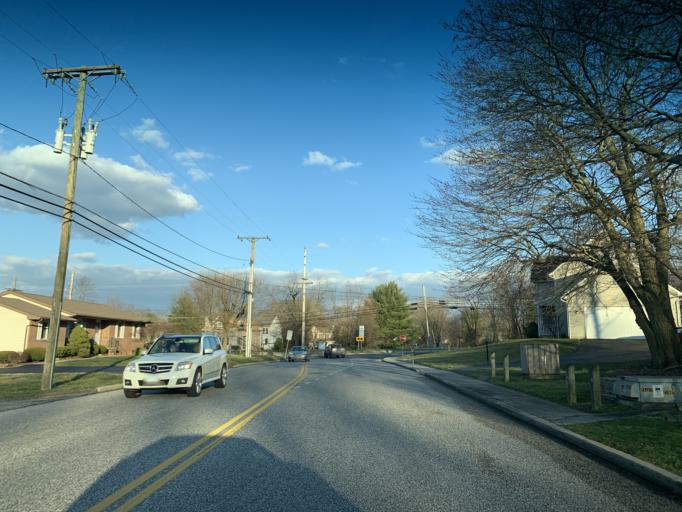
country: US
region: Maryland
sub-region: Harford County
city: Aberdeen
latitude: 39.5277
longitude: -76.1718
